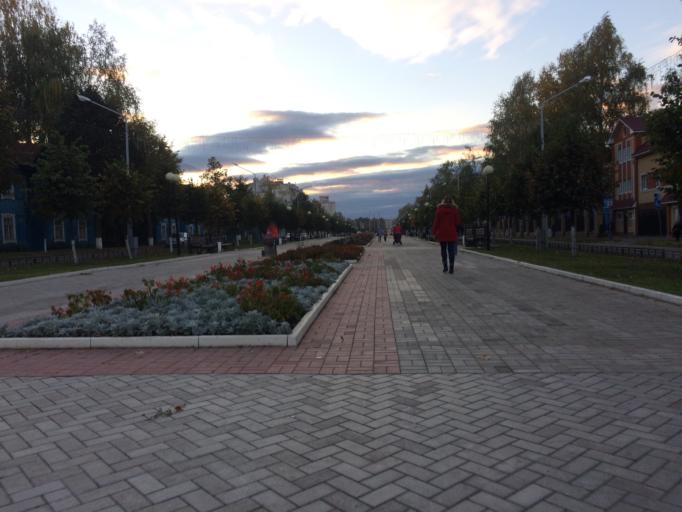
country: RU
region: Mariy-El
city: Yoshkar-Ola
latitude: 56.6393
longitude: 47.8766
